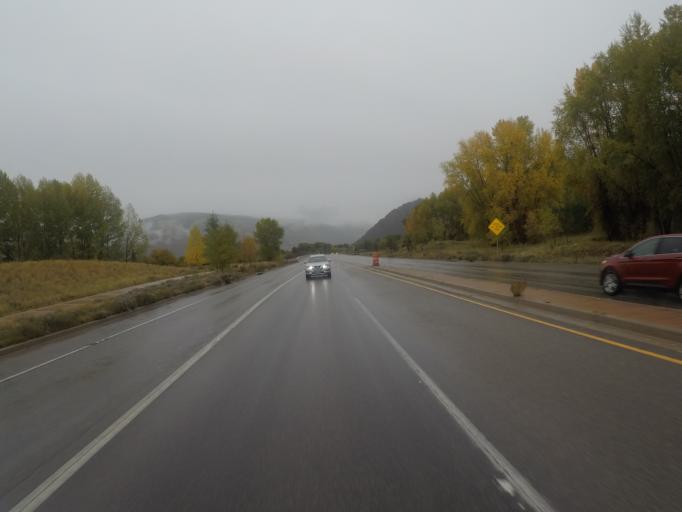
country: US
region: Colorado
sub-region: Pitkin County
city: Aspen
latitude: 39.2025
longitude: -106.8519
